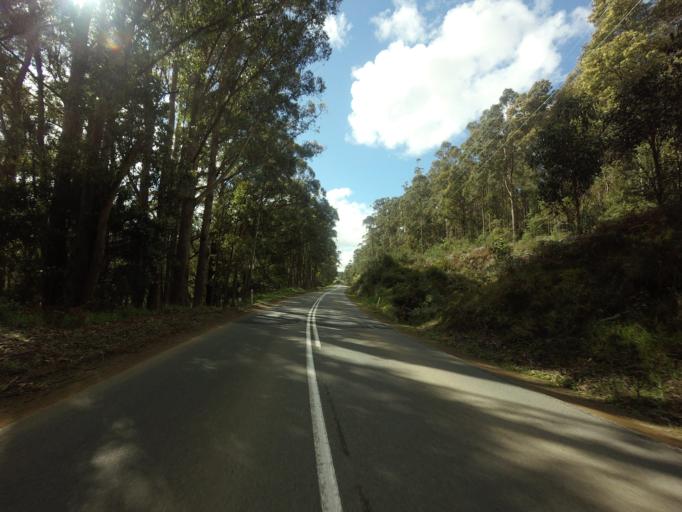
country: AU
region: Tasmania
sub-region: Huon Valley
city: Geeveston
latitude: -43.2265
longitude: 146.9877
